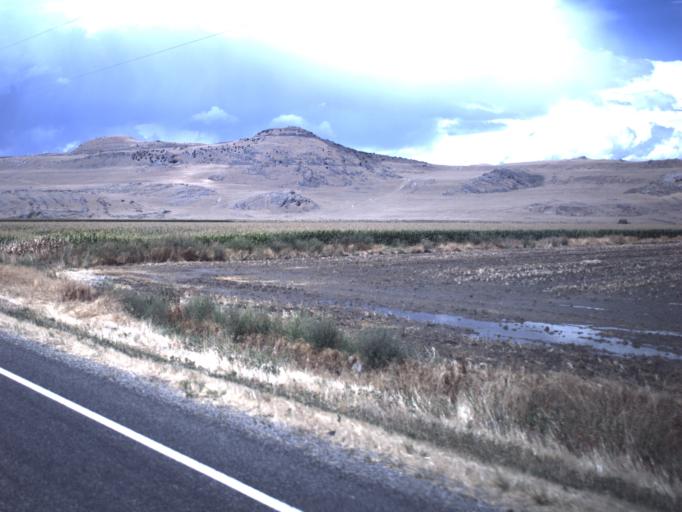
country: US
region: Utah
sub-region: Box Elder County
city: Elwood
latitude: 41.5713
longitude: -112.2076
